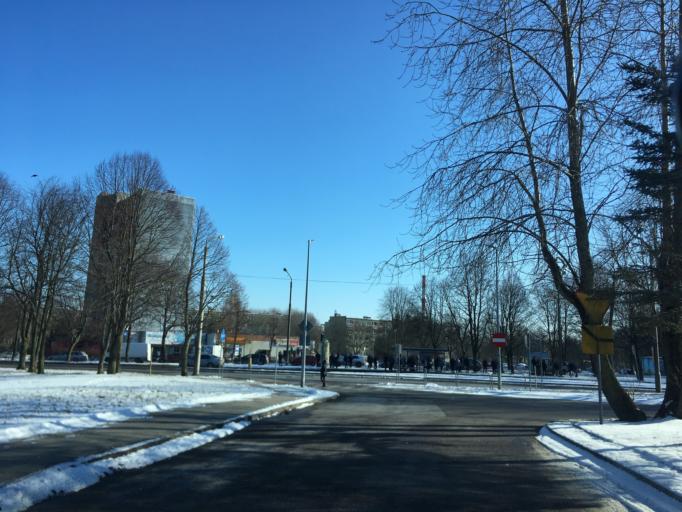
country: PL
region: Pomeranian Voivodeship
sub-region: Powiat slupski
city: Kobylnica
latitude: 54.4594
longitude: 16.9960
